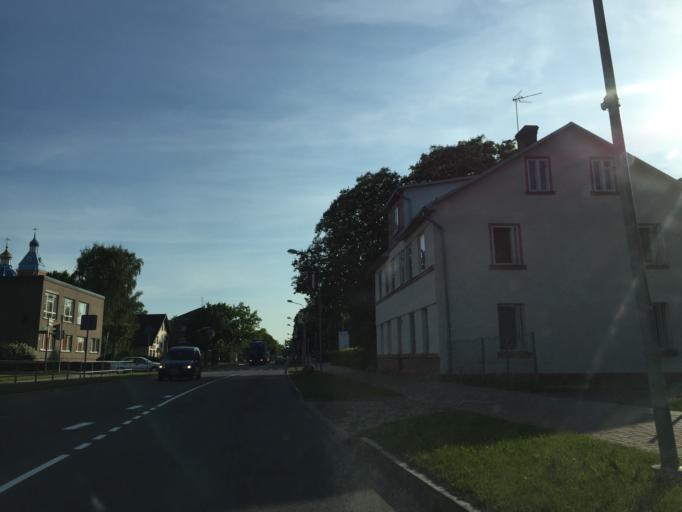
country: LV
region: Bauskas Rajons
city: Bauska
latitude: 56.4062
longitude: 24.1854
